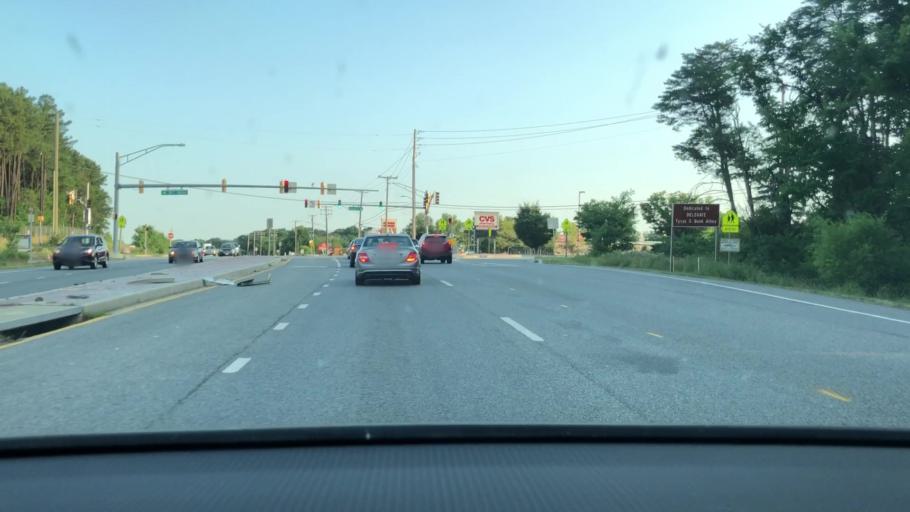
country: US
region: Maryland
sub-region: Anne Arundel County
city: Fort Meade
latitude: 39.1274
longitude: -76.7352
